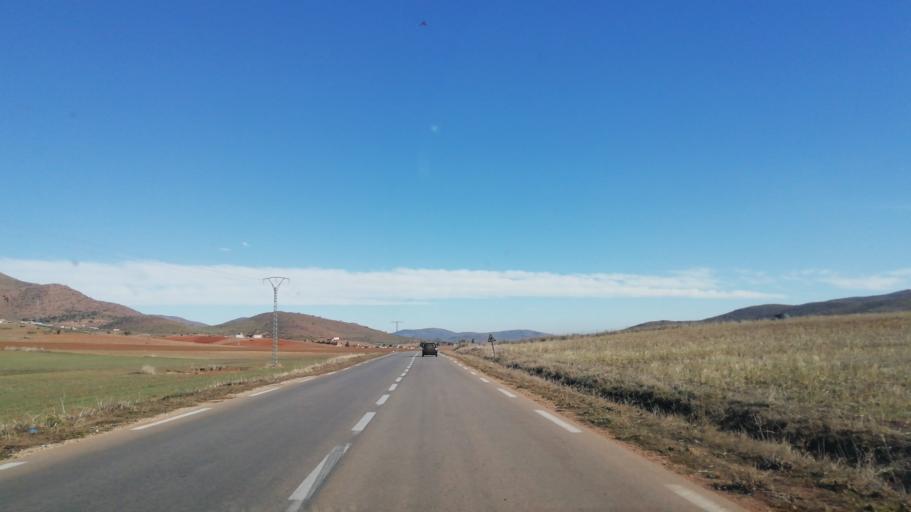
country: DZ
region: Tlemcen
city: Sebdou
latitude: 34.7347
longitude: -1.1758
